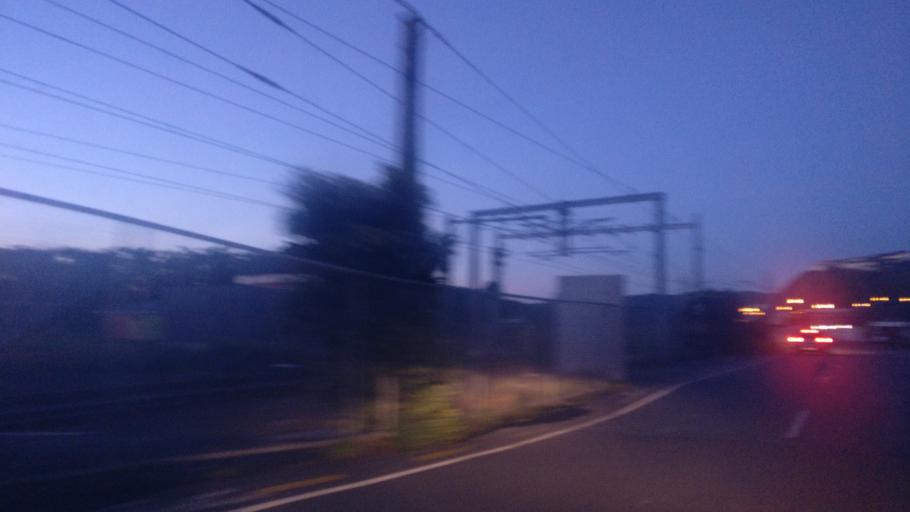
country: NZ
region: Wellington
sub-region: Porirua City
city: Porirua
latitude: -41.0946
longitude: 174.8682
